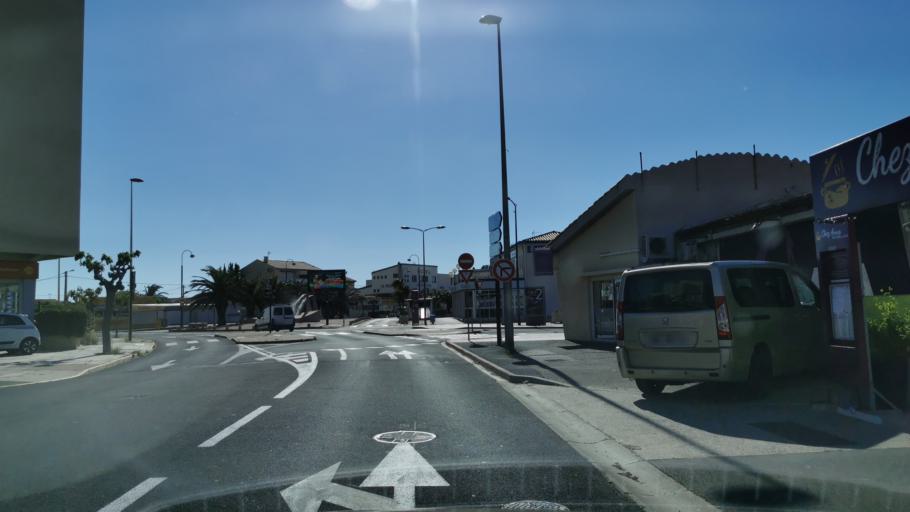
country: FR
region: Languedoc-Roussillon
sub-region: Departement de l'Aude
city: Armissan
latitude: 43.1597
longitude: 3.1650
